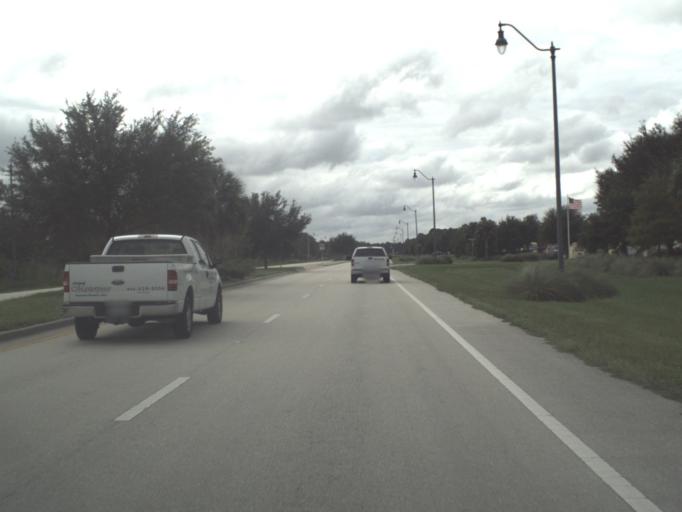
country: US
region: Florida
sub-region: Sarasota County
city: North Port
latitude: 27.0854
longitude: -82.1556
